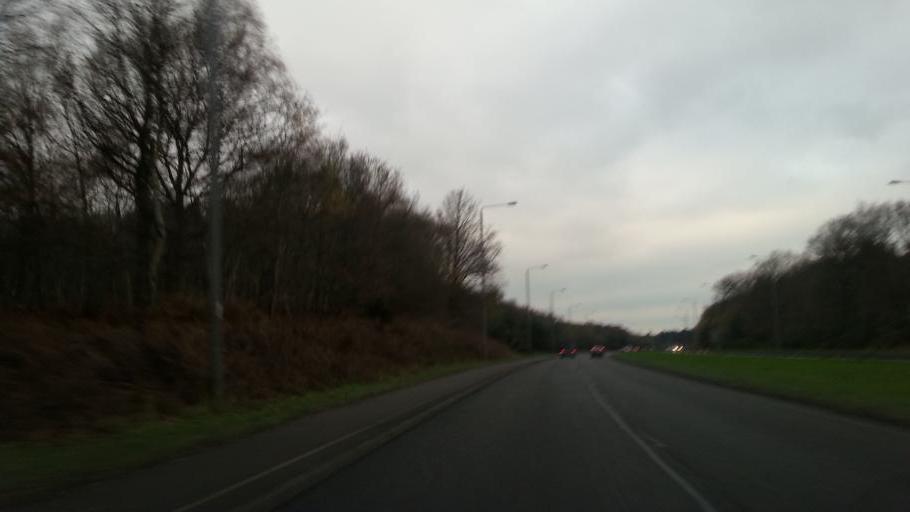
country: GB
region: England
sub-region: Nottinghamshire
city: Rainworth
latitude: 53.1235
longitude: -1.1200
